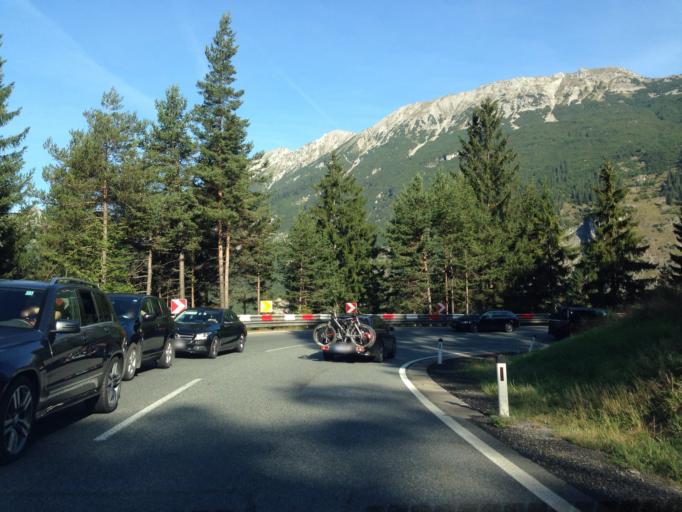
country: AT
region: Tyrol
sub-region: Politischer Bezirk Imst
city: Nassereith
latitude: 47.3590
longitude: 10.8546
